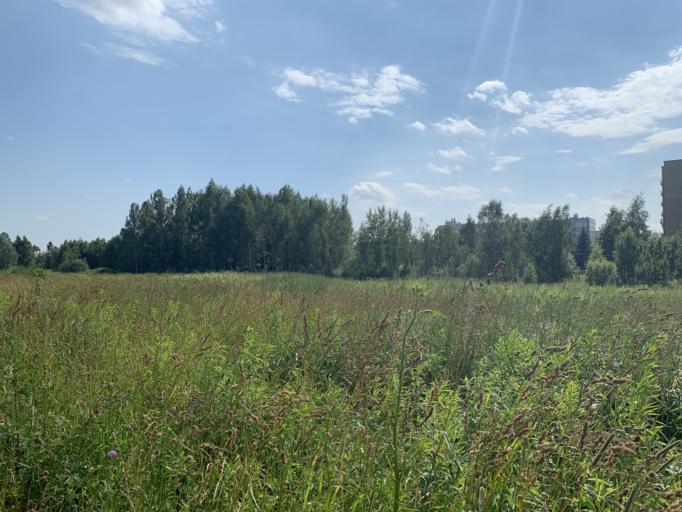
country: RU
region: Moskovskaya
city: Cherkizovo
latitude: 55.9721
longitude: 37.7952
